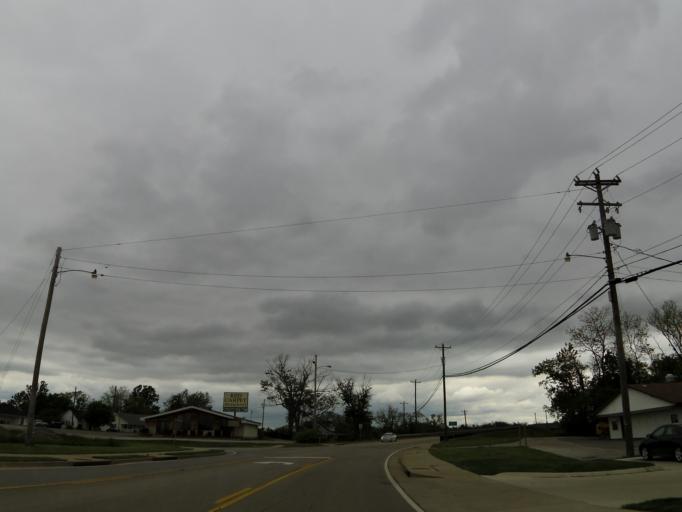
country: US
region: Kentucky
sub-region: Grant County
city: Williamstown
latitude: 38.6293
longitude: -84.5684
